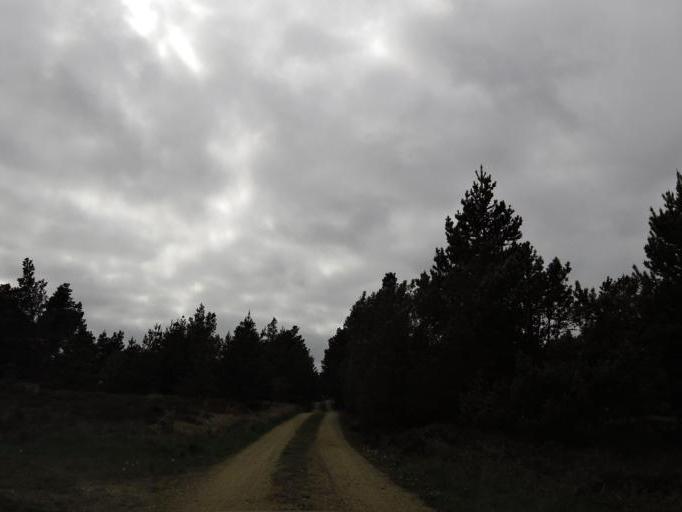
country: DE
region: Schleswig-Holstein
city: List
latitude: 55.1156
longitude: 8.5525
